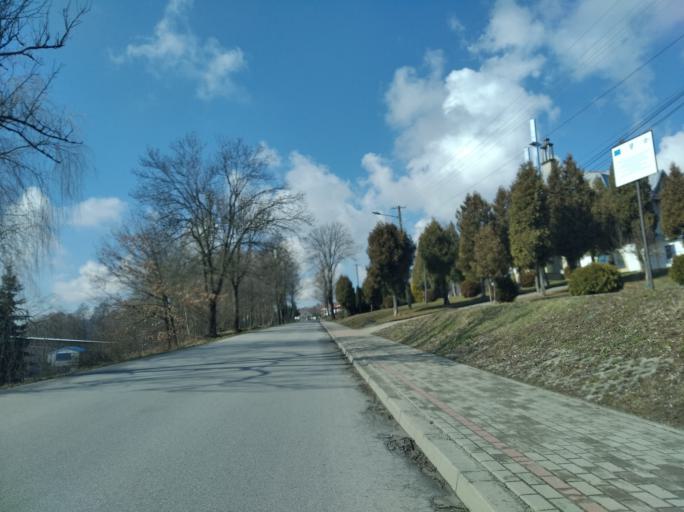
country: PL
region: Subcarpathian Voivodeship
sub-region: Powiat strzyzowski
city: Frysztak
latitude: 49.8734
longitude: 21.5828
